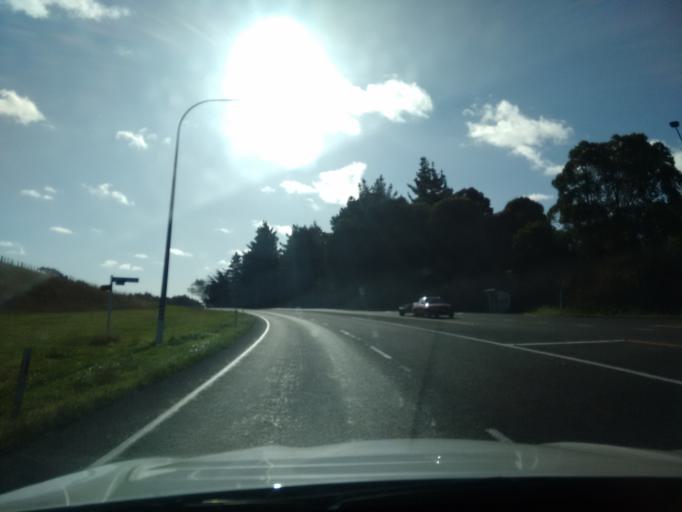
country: NZ
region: Manawatu-Wanganui
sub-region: Wanganui District
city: Wanganui
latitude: -39.8372
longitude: 174.9163
